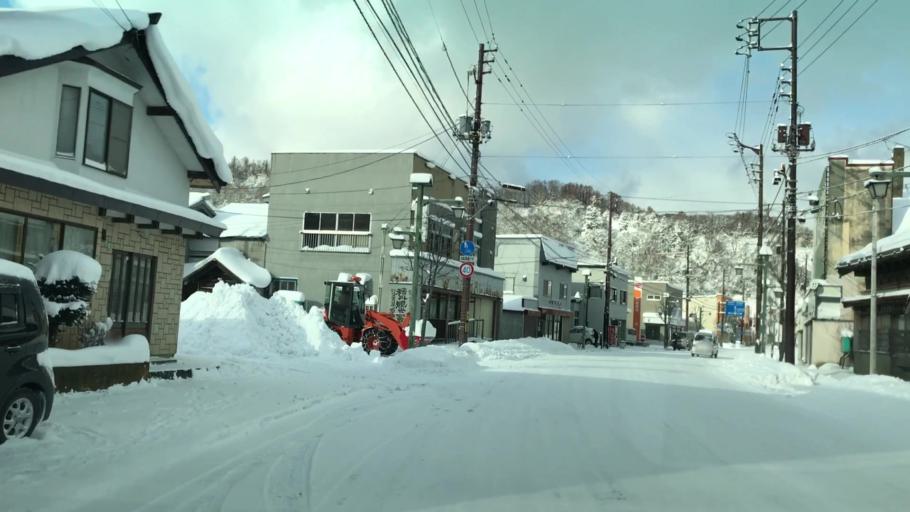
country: JP
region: Hokkaido
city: Yoichi
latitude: 43.2956
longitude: 140.6014
